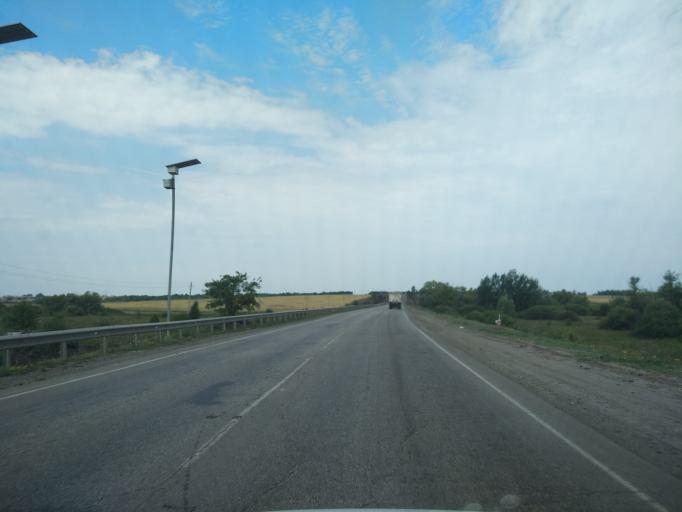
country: RU
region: Voronezj
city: Verkhnyaya Khava
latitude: 51.6750
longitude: 39.8179
